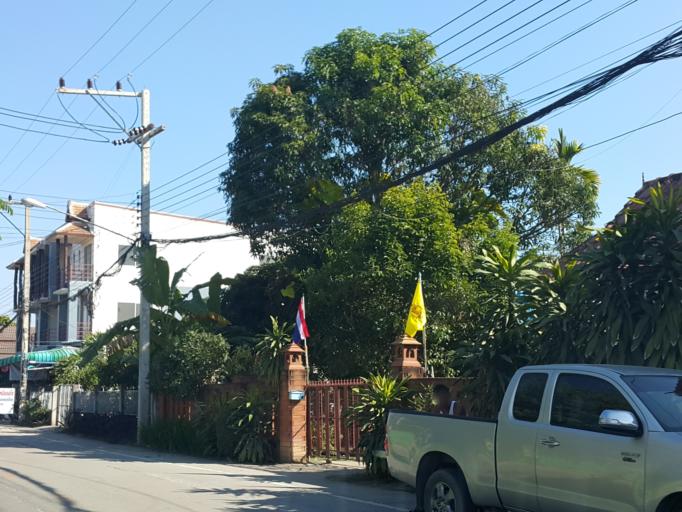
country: TH
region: Chiang Mai
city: San Sai
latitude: 18.8855
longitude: 99.0119
